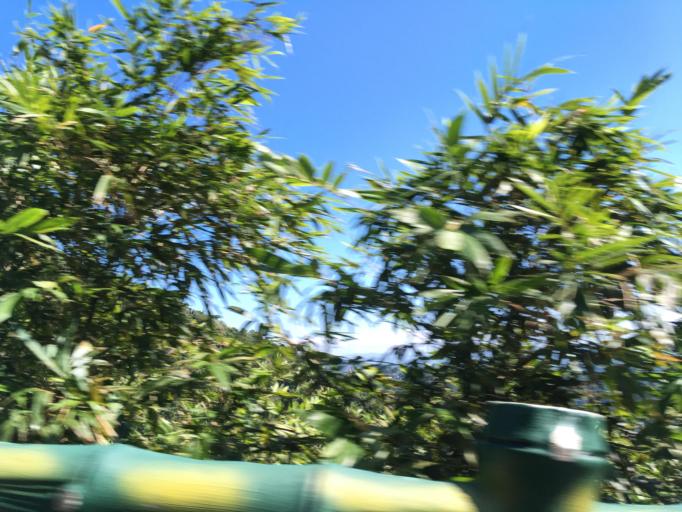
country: TW
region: Taipei
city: Taipei
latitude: 25.1547
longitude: 121.5044
